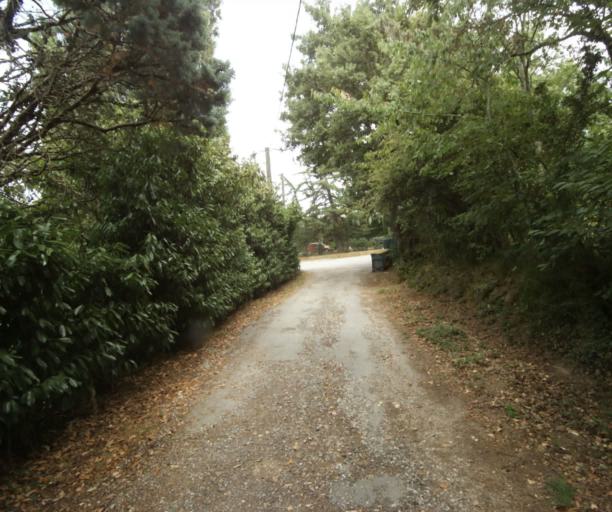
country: FR
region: Midi-Pyrenees
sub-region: Departement de la Haute-Garonne
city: Revel
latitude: 43.4510
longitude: 2.0267
